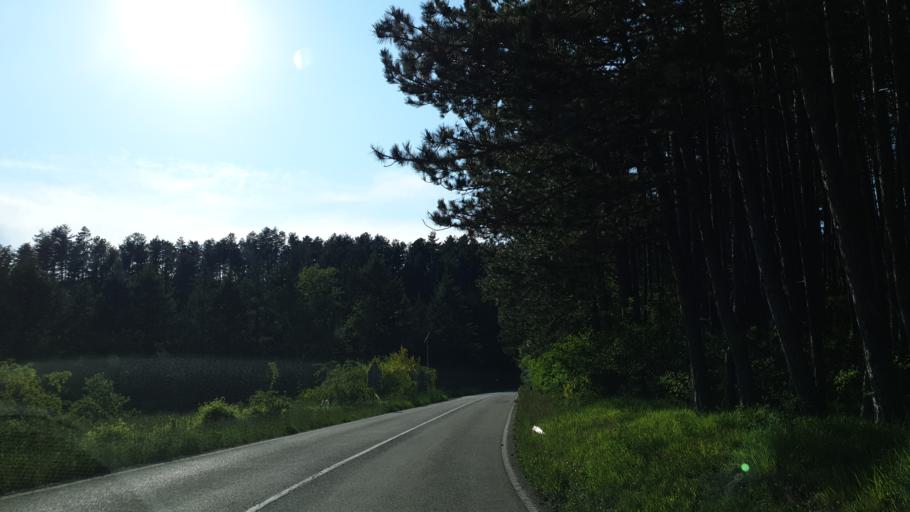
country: IT
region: Tuscany
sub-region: Province of Arezzo
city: Montemignaio
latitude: 43.7848
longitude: 11.6064
